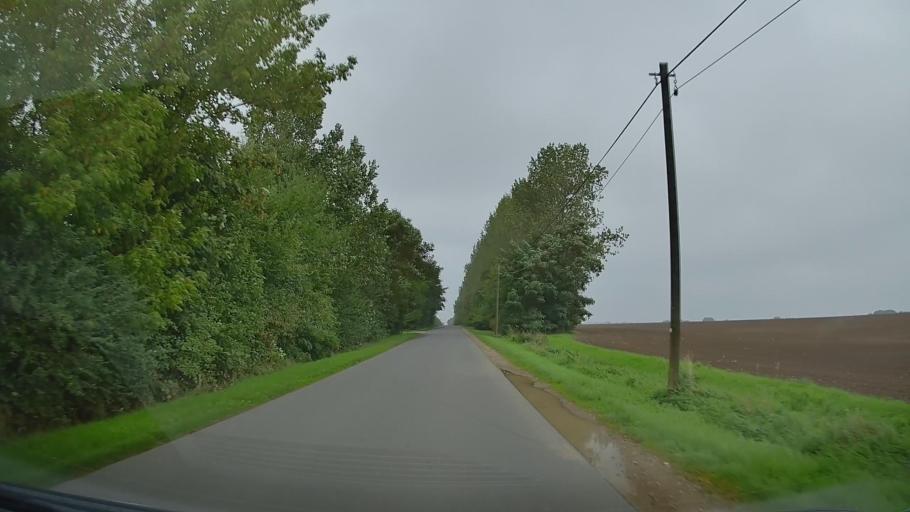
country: DE
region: Mecklenburg-Vorpommern
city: Neubukow
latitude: 54.0459
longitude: 11.6194
